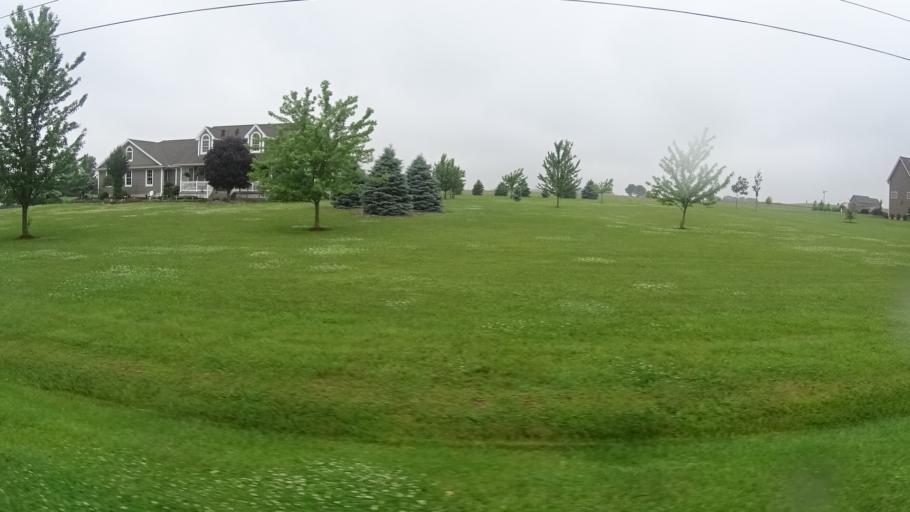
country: US
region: Ohio
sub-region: Huron County
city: Bellevue
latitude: 41.3270
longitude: -82.8430
